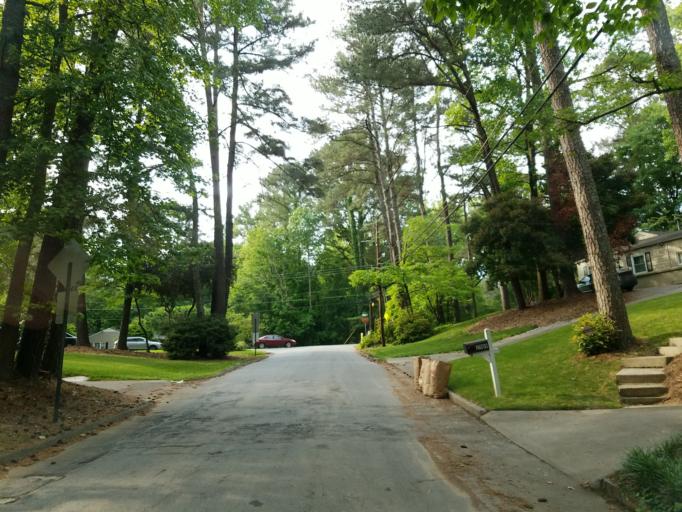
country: US
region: Georgia
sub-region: Cobb County
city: Vinings
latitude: 33.8237
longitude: -84.4464
